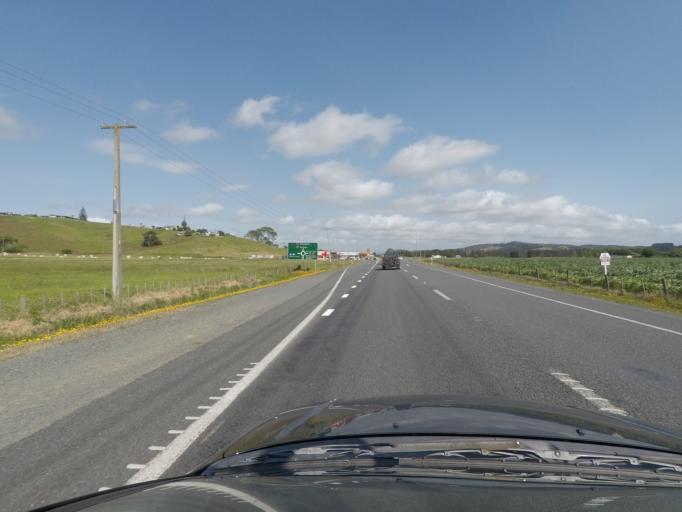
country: NZ
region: Northland
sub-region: Whangarei
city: Ruakaka
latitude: -35.8939
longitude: 174.4359
